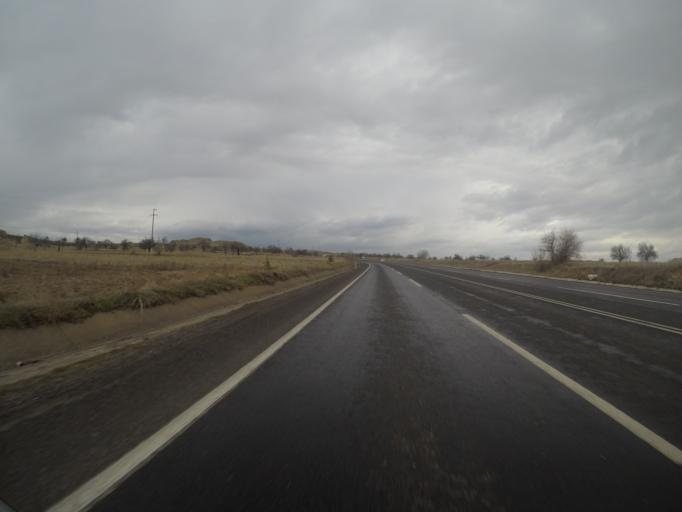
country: TR
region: Nevsehir
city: Urgub
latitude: 38.6351
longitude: 34.8761
